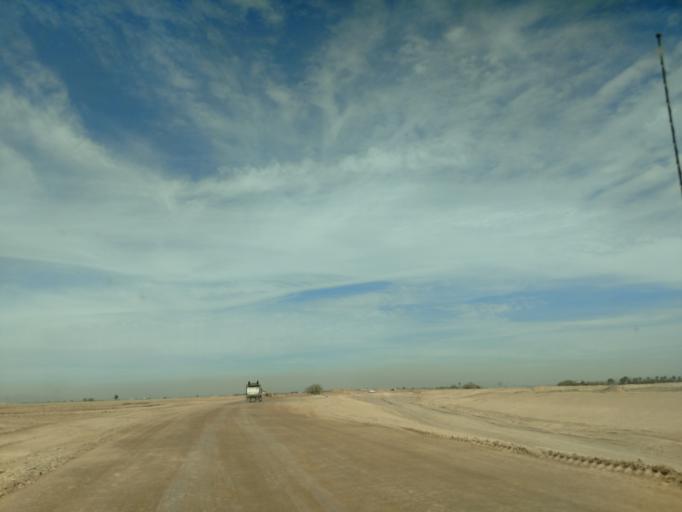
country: US
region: Arizona
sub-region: Maricopa County
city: Laveen
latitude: 33.3508
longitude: -112.1897
